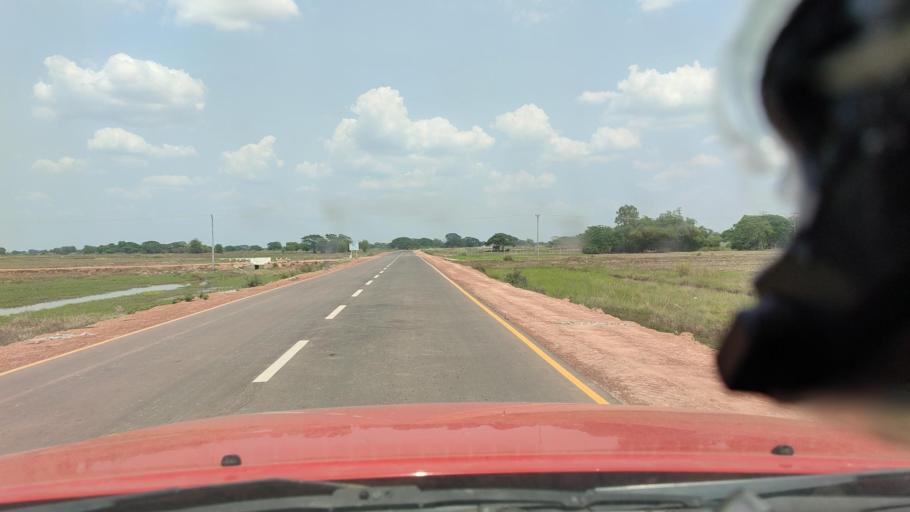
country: MM
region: Bago
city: Thanatpin
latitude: 17.0439
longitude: 96.3614
